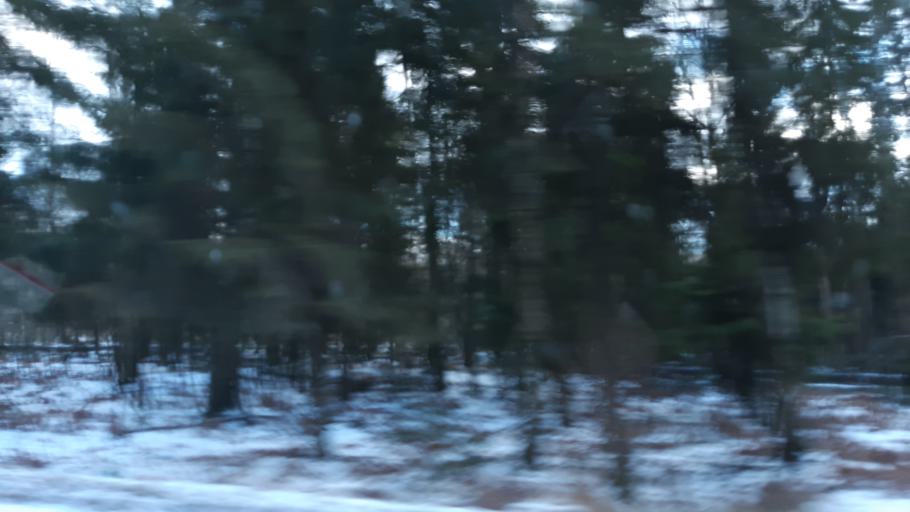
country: RU
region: Moskovskaya
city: Noginsk
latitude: 55.9333
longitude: 38.5449
